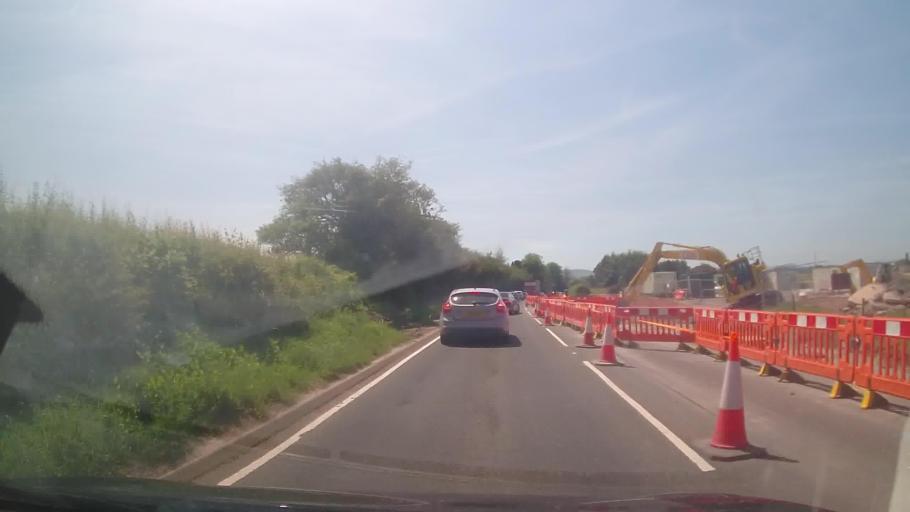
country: GB
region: England
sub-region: Herefordshire
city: Hereford
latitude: 52.0810
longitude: -2.7222
